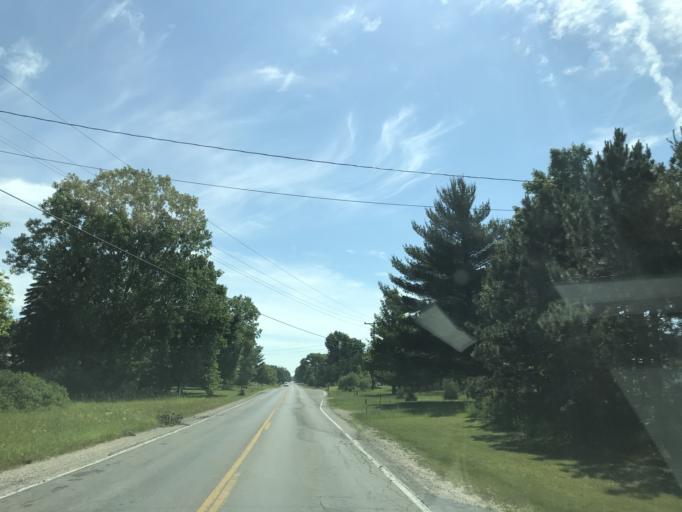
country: US
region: Michigan
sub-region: Grand Traverse County
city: Traverse City
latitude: 44.6576
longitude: -85.6694
